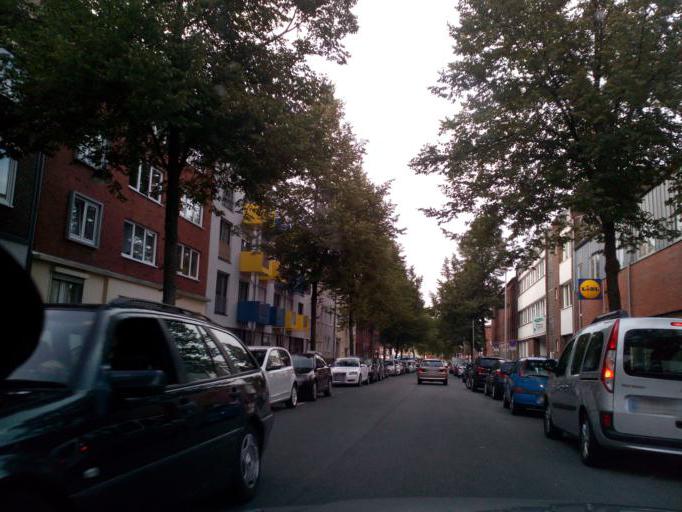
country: DE
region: North Rhine-Westphalia
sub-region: Regierungsbezirk Munster
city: Muenster
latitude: 51.9520
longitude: 7.6322
